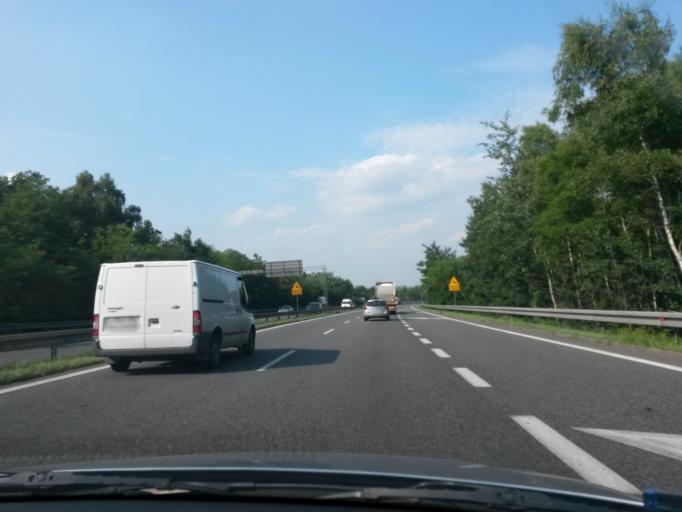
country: PL
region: Silesian Voivodeship
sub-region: Myslowice
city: Myslowice
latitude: 50.2111
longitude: 19.1672
